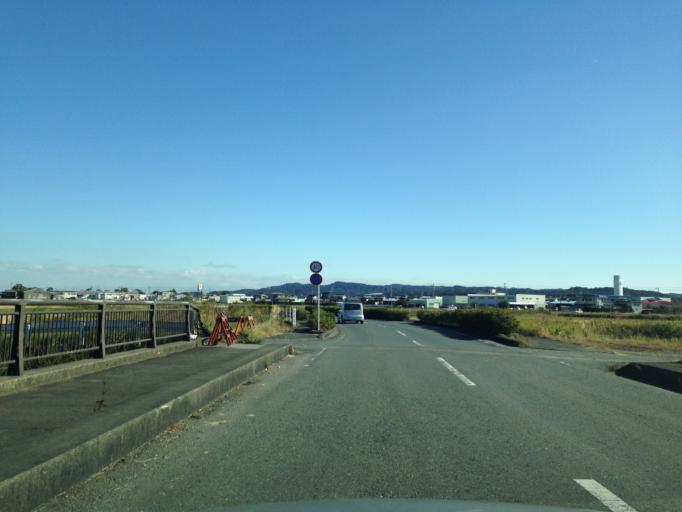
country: JP
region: Shizuoka
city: Fukuroi
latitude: 34.7550
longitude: 137.9258
